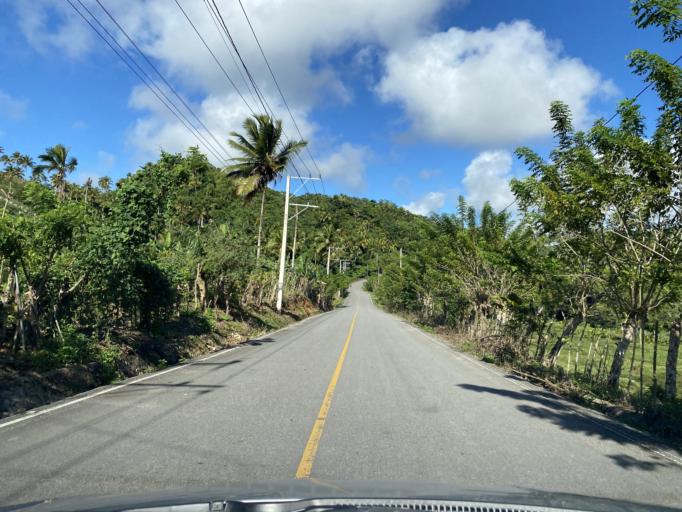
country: DO
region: Samana
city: Sanchez
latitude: 19.2541
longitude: -69.5810
